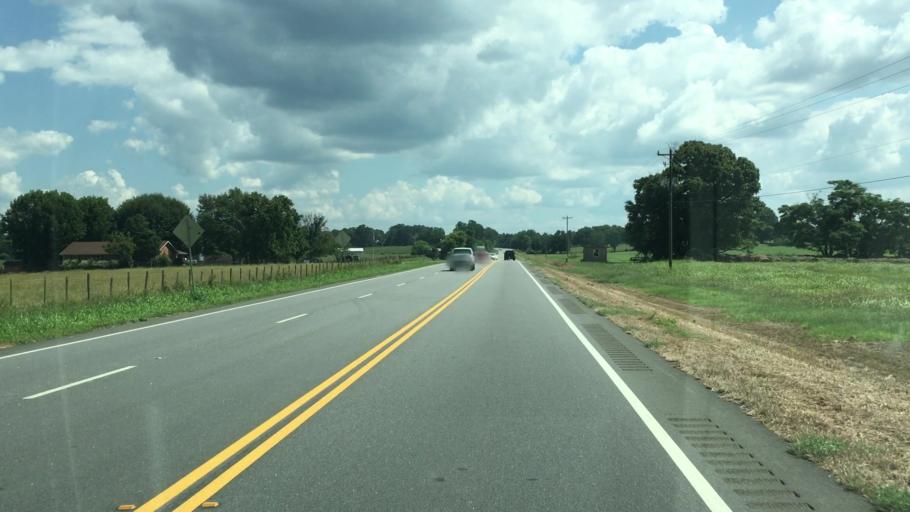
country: US
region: Georgia
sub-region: Morgan County
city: Madison
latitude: 33.4837
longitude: -83.4361
